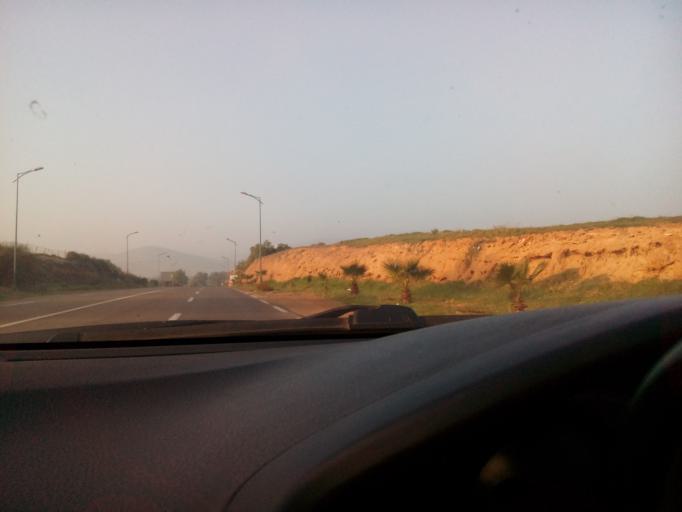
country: DZ
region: Oran
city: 'Ain el Turk
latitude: 35.7118
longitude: -0.8703
